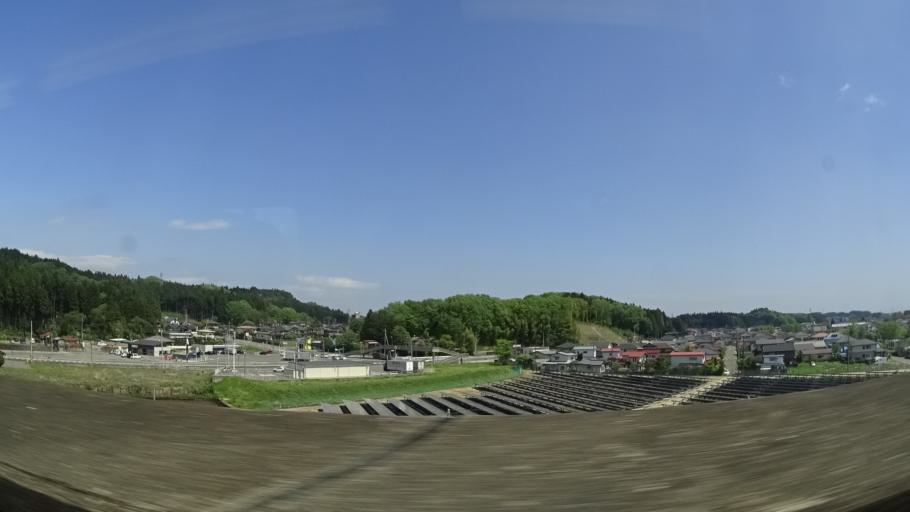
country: JP
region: Tochigi
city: Yaita
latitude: 36.7604
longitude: 139.9434
